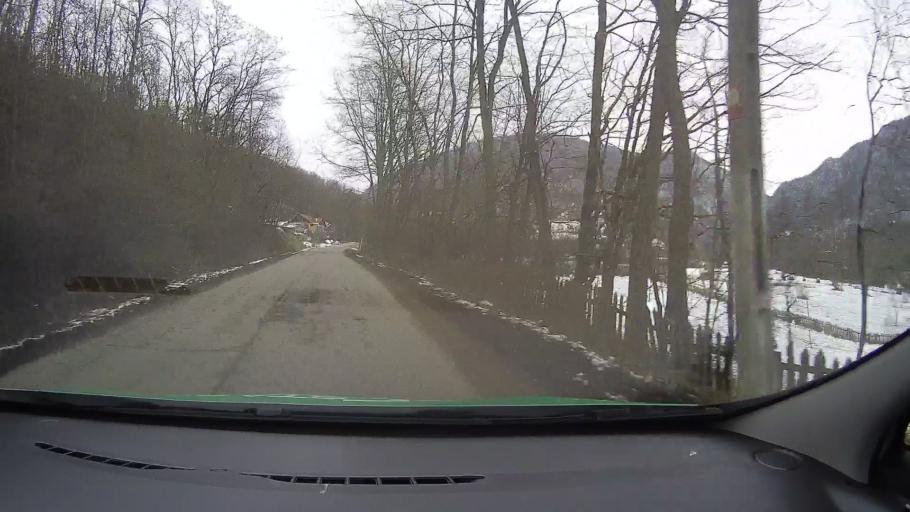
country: RO
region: Hunedoara
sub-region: Comuna Balsa
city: Balsa
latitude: 46.0229
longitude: 23.1187
